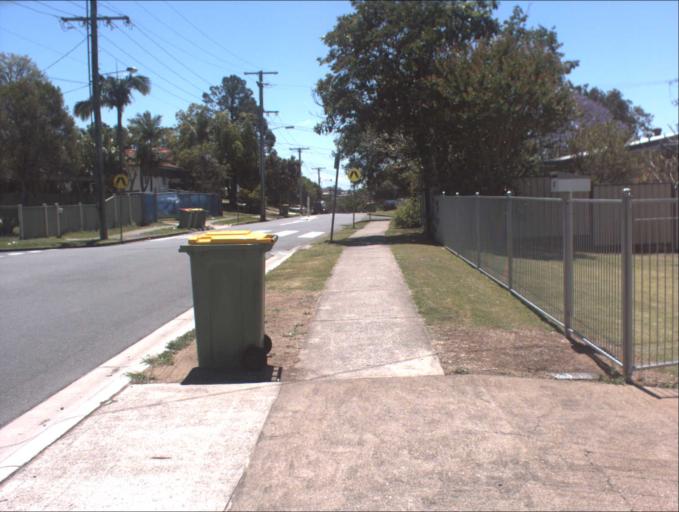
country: AU
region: Queensland
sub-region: Logan
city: Woodridge
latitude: -27.6268
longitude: 153.1074
